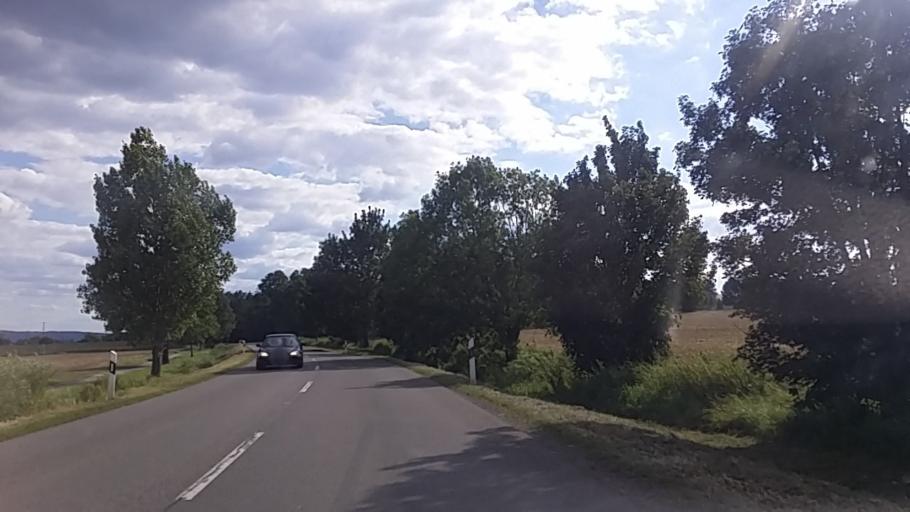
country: HU
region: Baranya
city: Sasd
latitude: 46.2969
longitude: 18.1236
